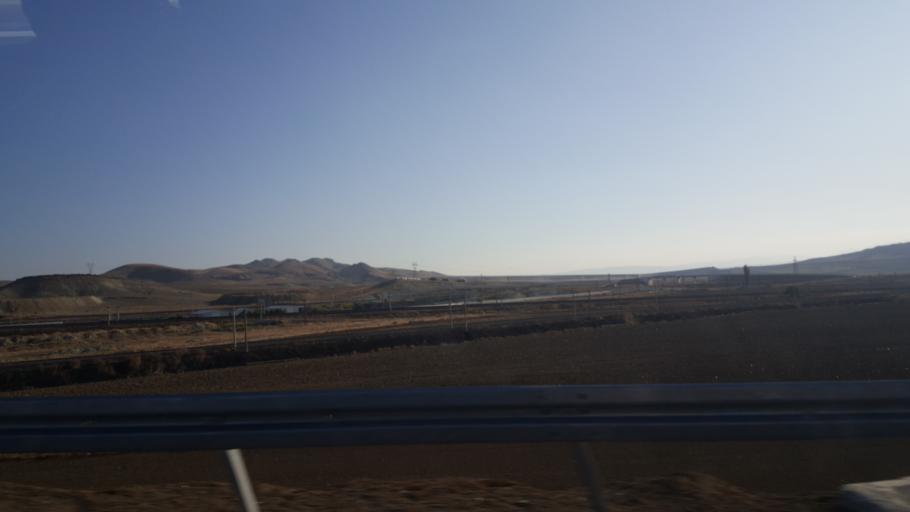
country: TR
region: Ankara
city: Polatli
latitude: 39.5738
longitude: 32.0323
